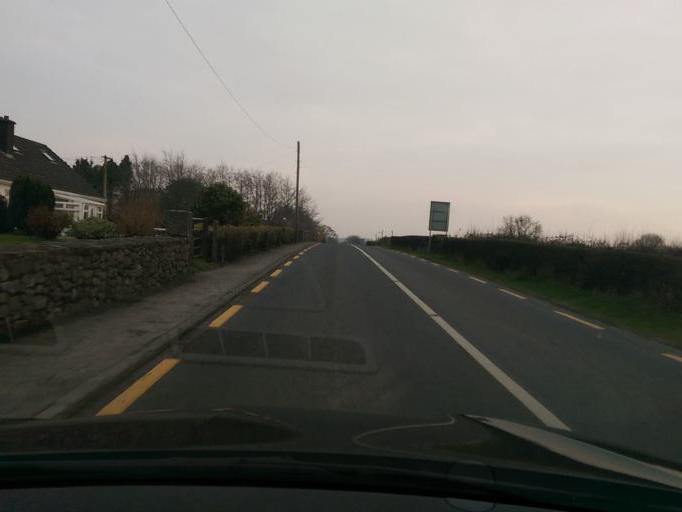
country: IE
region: Leinster
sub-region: An Longfort
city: Ballymahon
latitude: 53.5315
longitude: -7.7921
